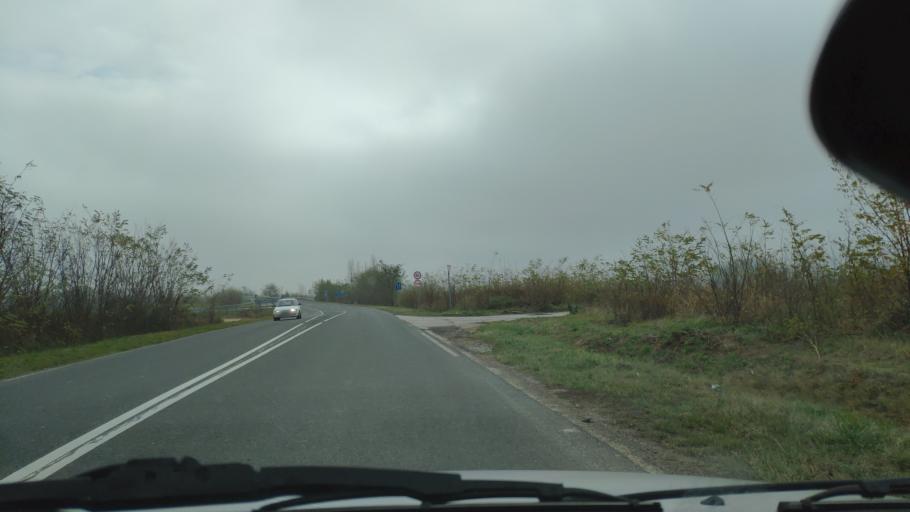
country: HU
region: Somogy
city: Balatonbereny
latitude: 46.6525
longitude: 17.2977
